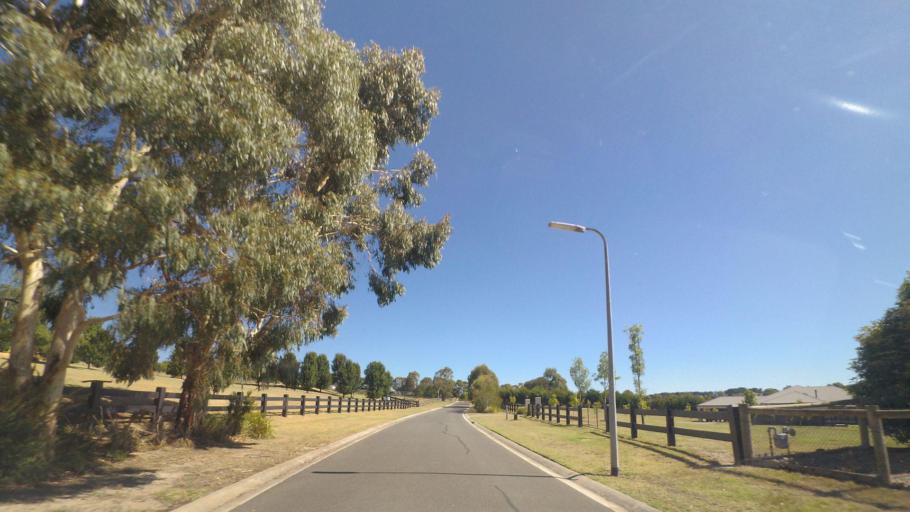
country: AU
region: Victoria
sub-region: Yarra Ranges
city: Chirnside Park
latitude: -37.7466
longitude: 145.3133
